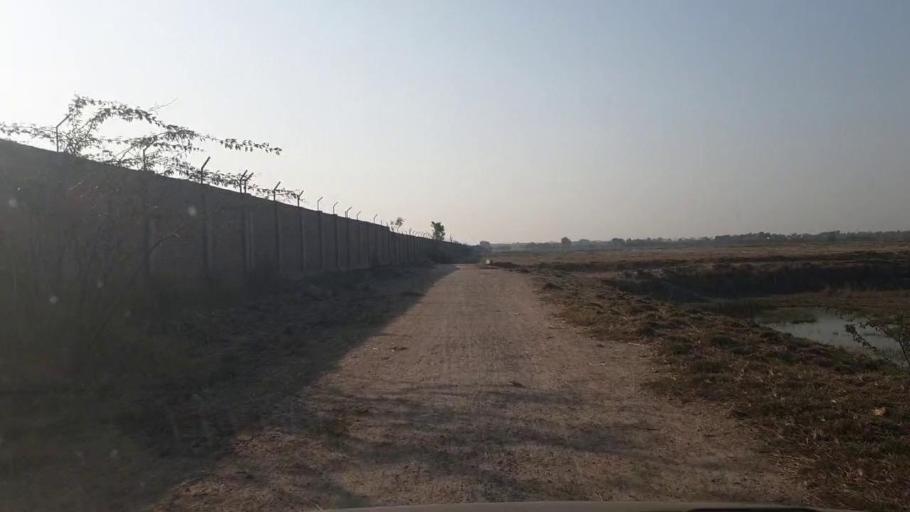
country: PK
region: Sindh
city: Tando Adam
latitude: 25.7470
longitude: 68.6400
